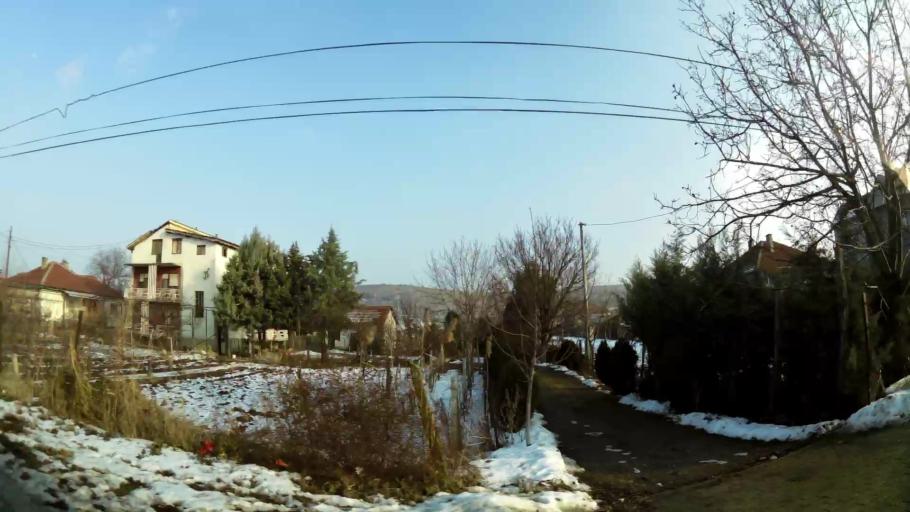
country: MK
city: Miladinovci
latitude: 41.9864
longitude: 21.6515
